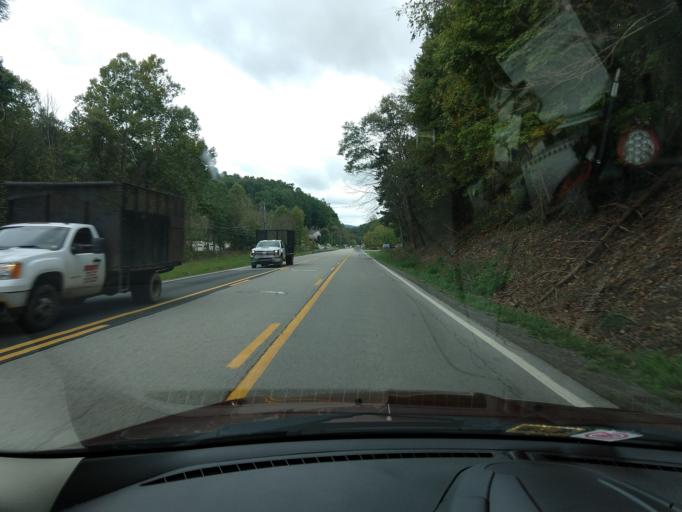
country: US
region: West Virginia
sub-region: Barbour County
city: Philippi
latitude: 39.1318
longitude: -80.0129
